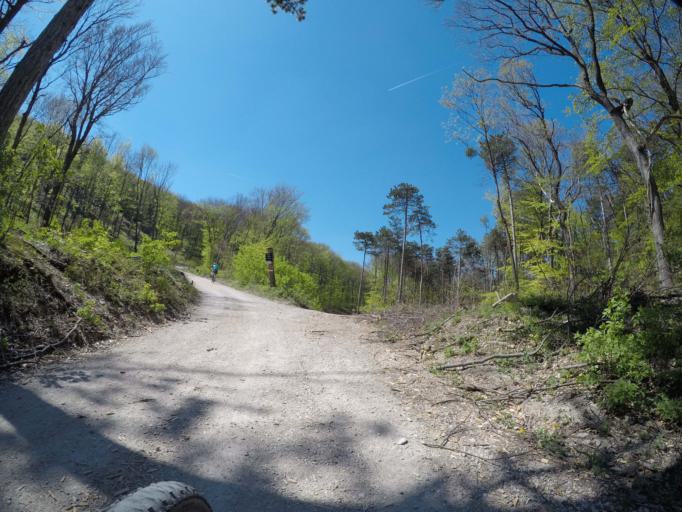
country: AT
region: Lower Austria
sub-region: Politischer Bezirk Modling
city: Hinterbruehl
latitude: 48.0621
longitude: 16.2547
